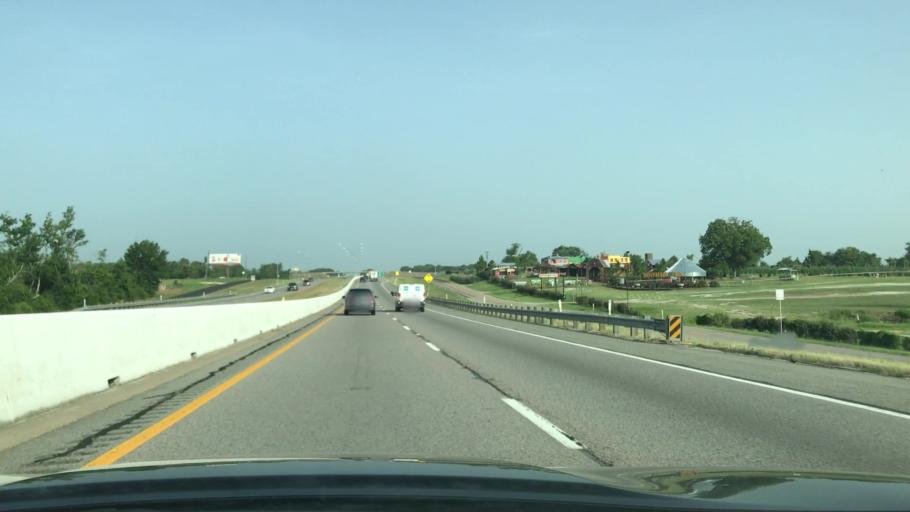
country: US
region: Texas
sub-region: Van Zandt County
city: Canton
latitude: 32.5665
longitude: -95.8249
